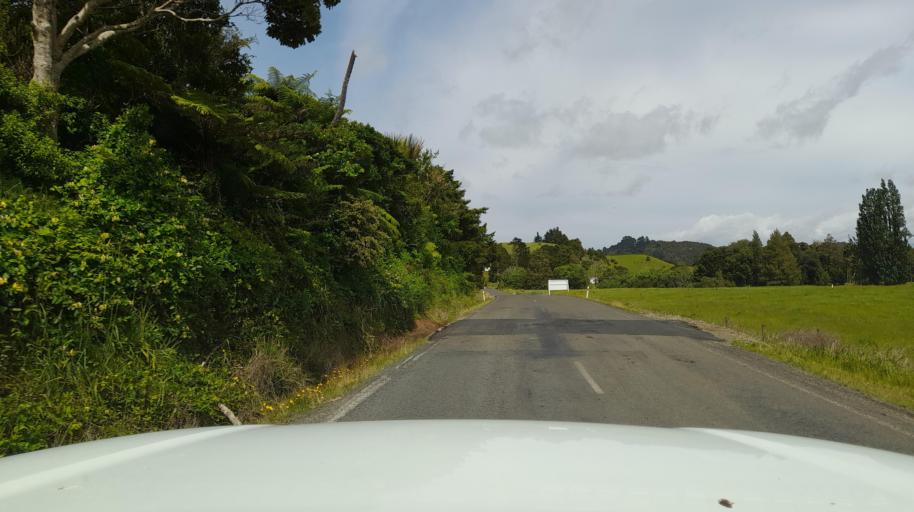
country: NZ
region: Northland
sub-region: Far North District
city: Kaitaia
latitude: -35.2648
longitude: 173.3776
